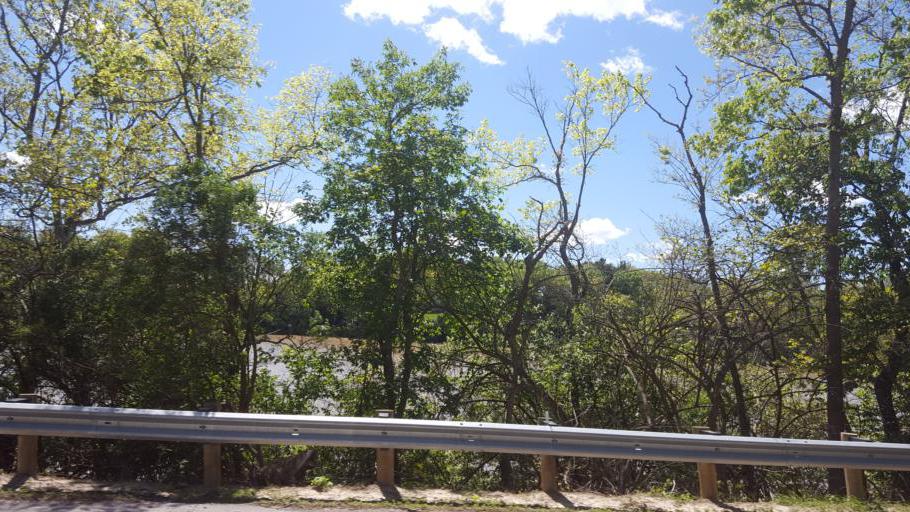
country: US
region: Ohio
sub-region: Franklin County
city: Dublin
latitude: 40.0569
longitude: -83.0990
